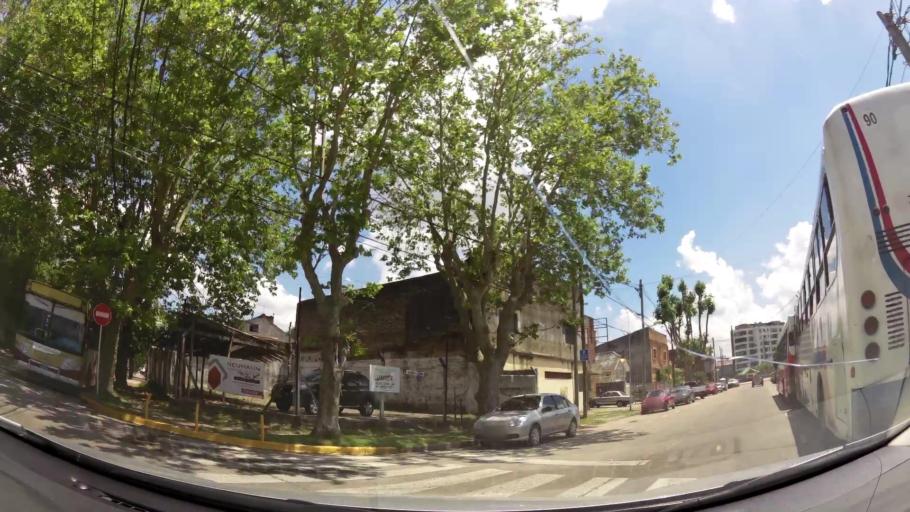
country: AR
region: Buenos Aires
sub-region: Partido de Tigre
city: Tigre
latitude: -34.4101
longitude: -58.5910
